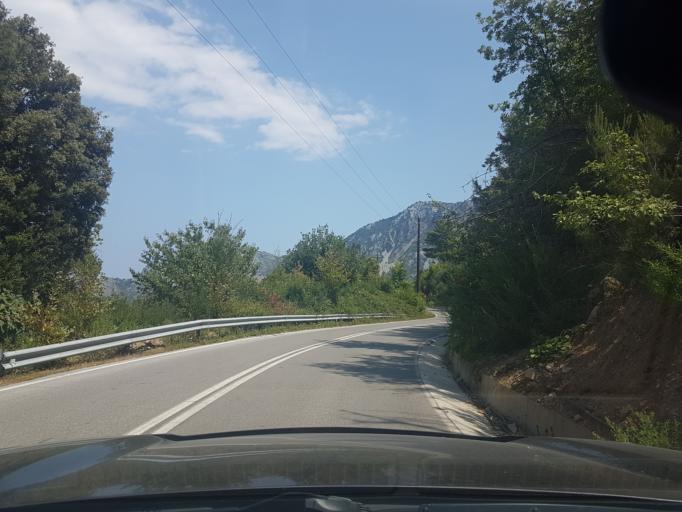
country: GR
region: Central Greece
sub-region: Nomos Evvoias
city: Kymi
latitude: 38.6386
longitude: 23.9427
